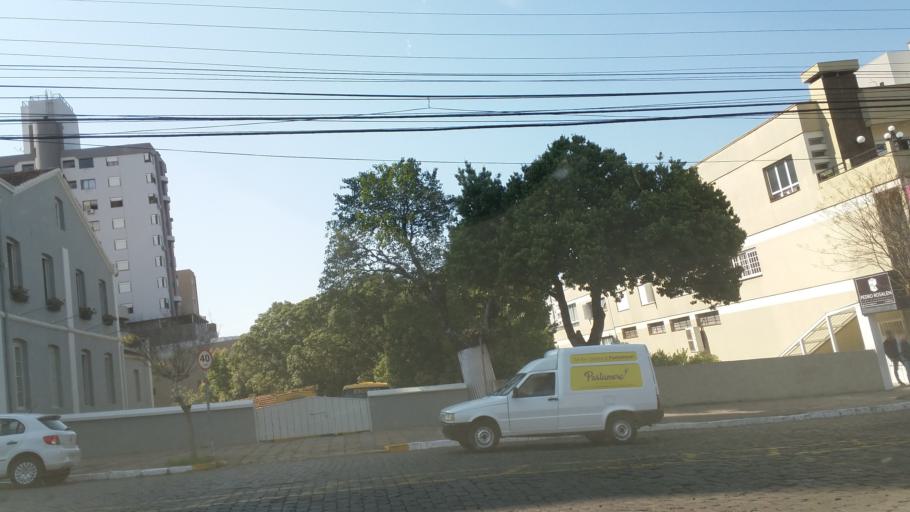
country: BR
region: Rio Grande do Sul
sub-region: Guapore
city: Guapore
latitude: -28.8485
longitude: -51.8900
